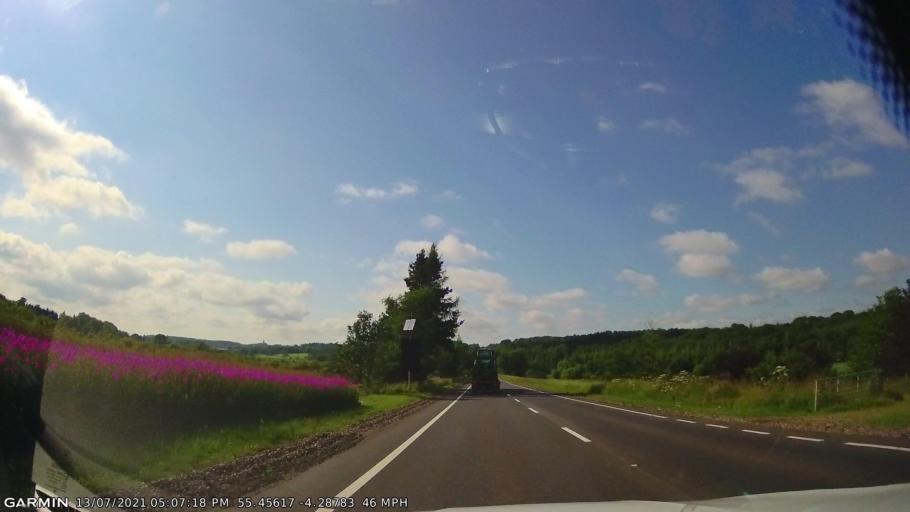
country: GB
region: Scotland
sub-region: East Ayrshire
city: Auchinleck
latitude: 55.4561
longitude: -4.2875
